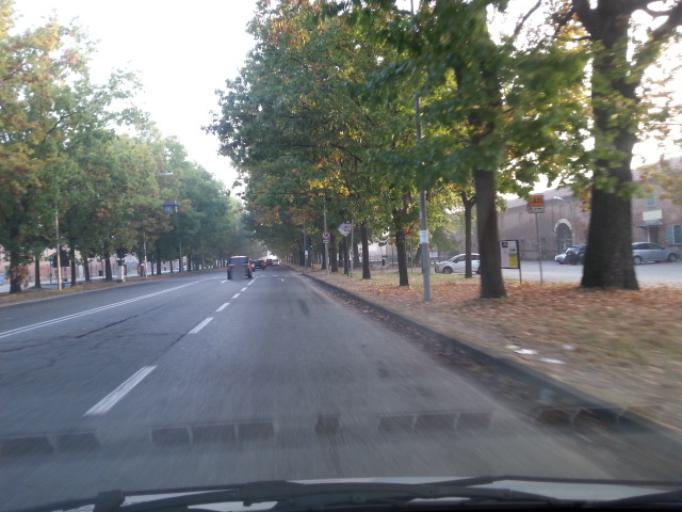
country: IT
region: Piedmont
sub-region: Provincia di Torino
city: Garino
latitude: 44.9975
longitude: 7.6071
